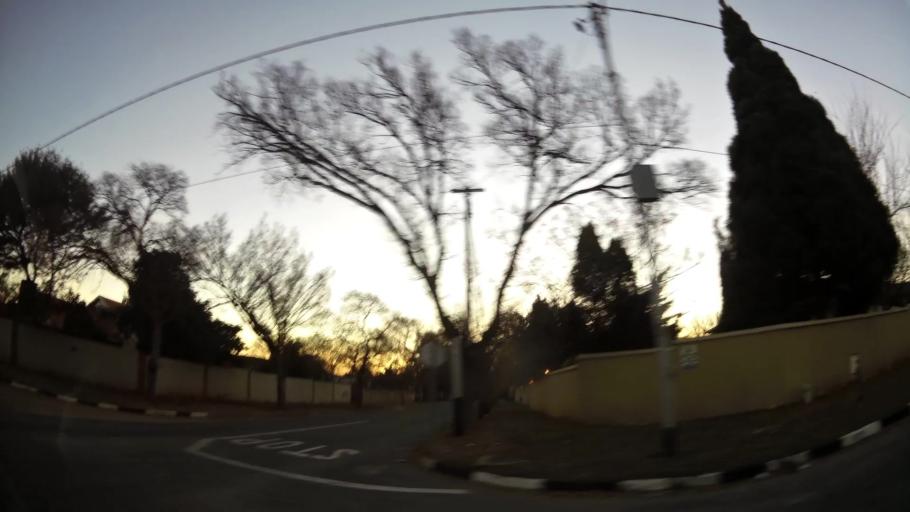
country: ZA
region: Gauteng
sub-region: City of Johannesburg Metropolitan Municipality
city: Roodepoort
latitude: -26.1706
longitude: 27.9159
